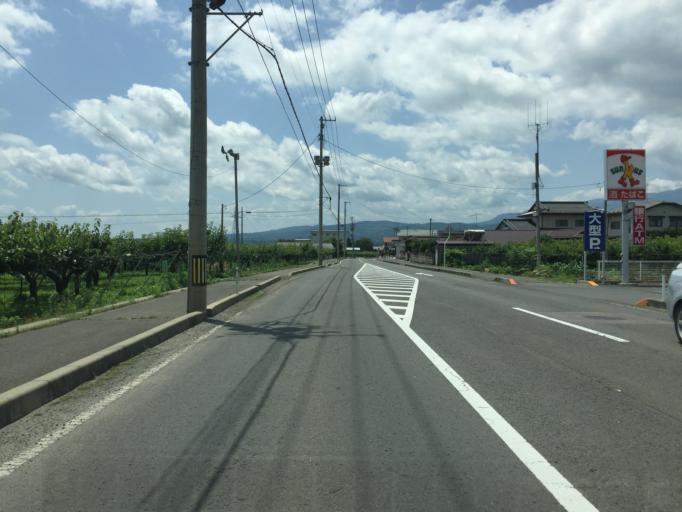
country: JP
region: Fukushima
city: Fukushima-shi
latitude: 37.7690
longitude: 140.4021
